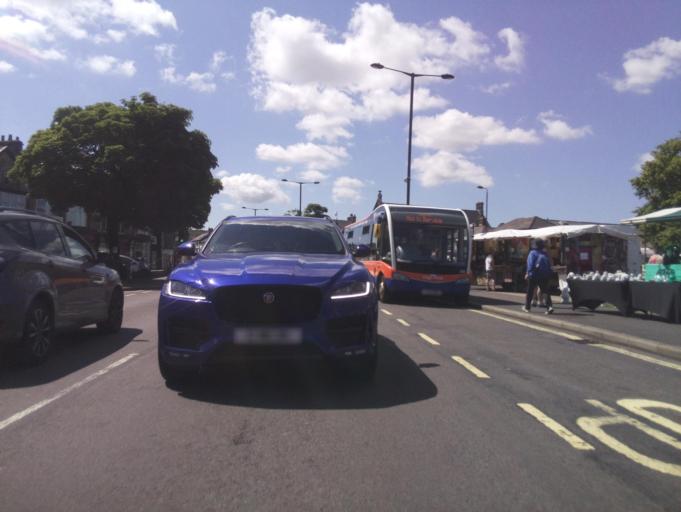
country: GB
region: England
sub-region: Derbyshire
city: Buxton
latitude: 53.2561
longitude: -1.9144
